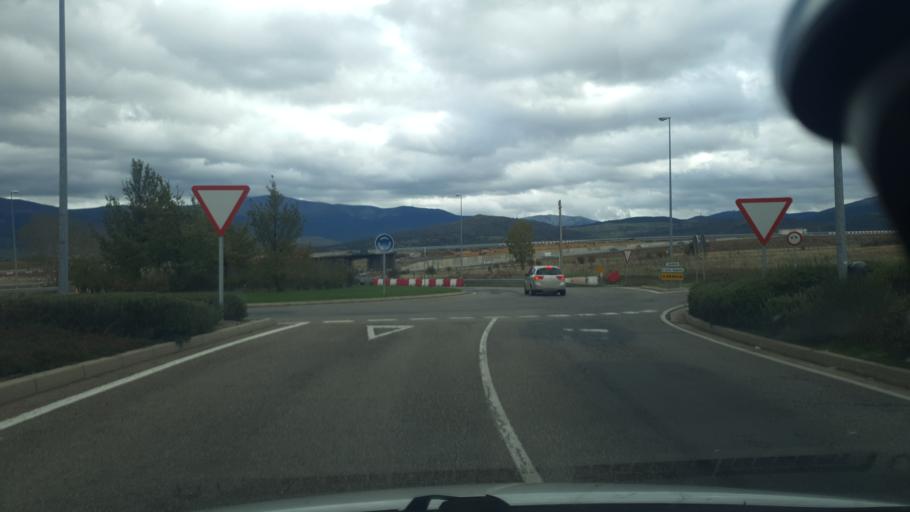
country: ES
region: Castille and Leon
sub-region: Provincia de Segovia
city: San Cristobal de Segovia
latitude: 40.9294
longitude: -4.0899
